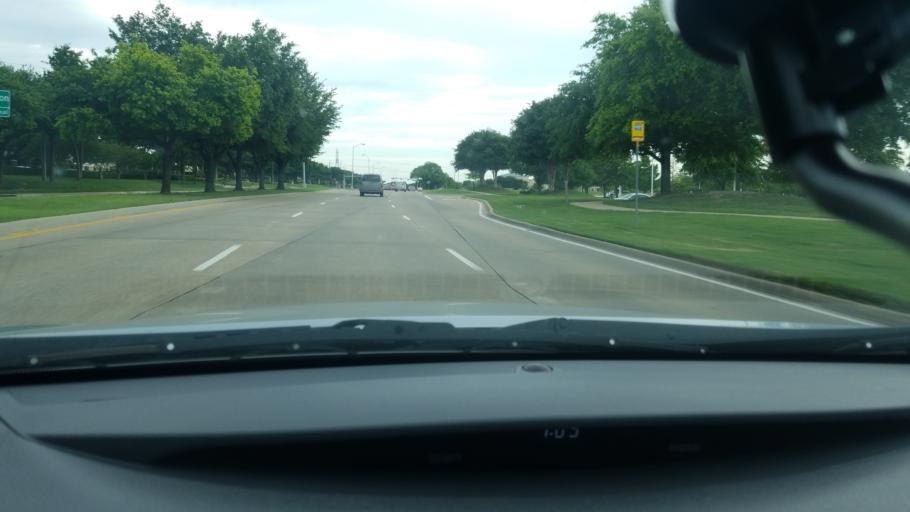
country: US
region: Texas
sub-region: Collin County
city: Frisco
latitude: 33.0678
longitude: -96.7963
